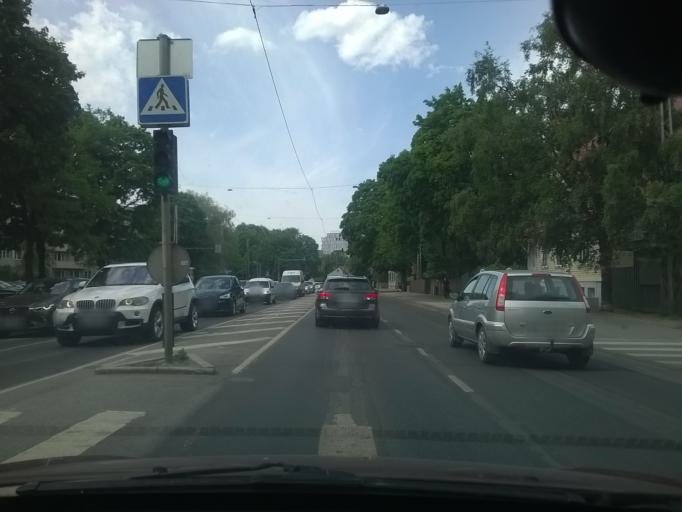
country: EE
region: Harju
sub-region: Tallinna linn
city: Tallinn
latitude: 59.4278
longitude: 24.7155
